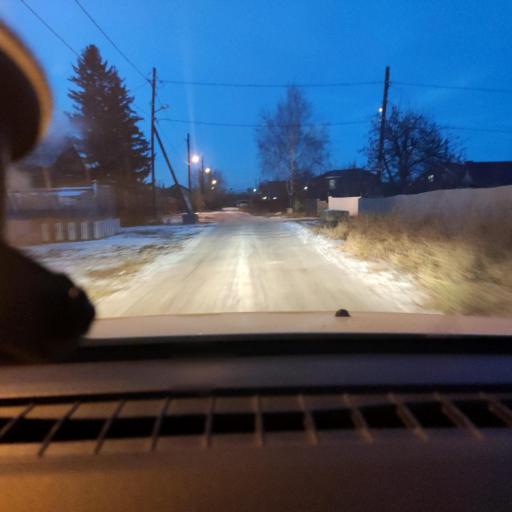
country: RU
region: Samara
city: Smyshlyayevka
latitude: 53.2551
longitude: 50.3555
